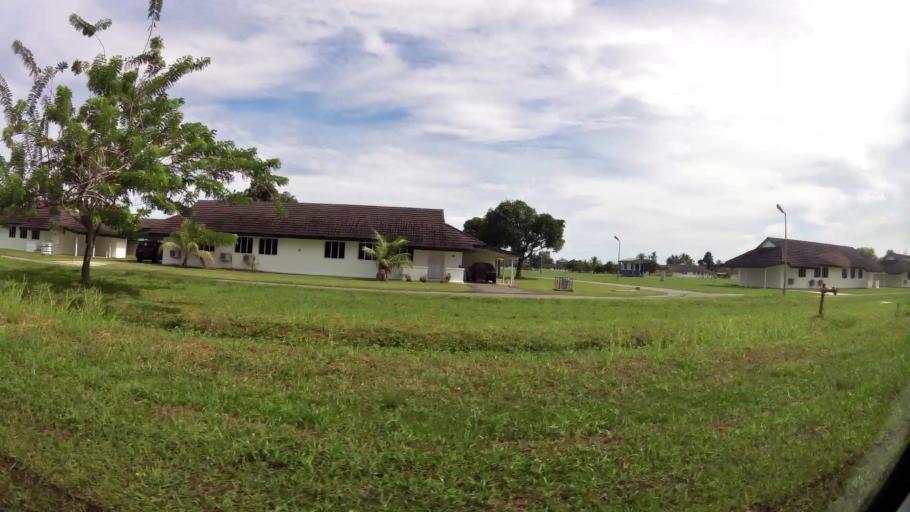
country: BN
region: Belait
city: Seria
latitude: 4.6050
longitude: 114.3227
